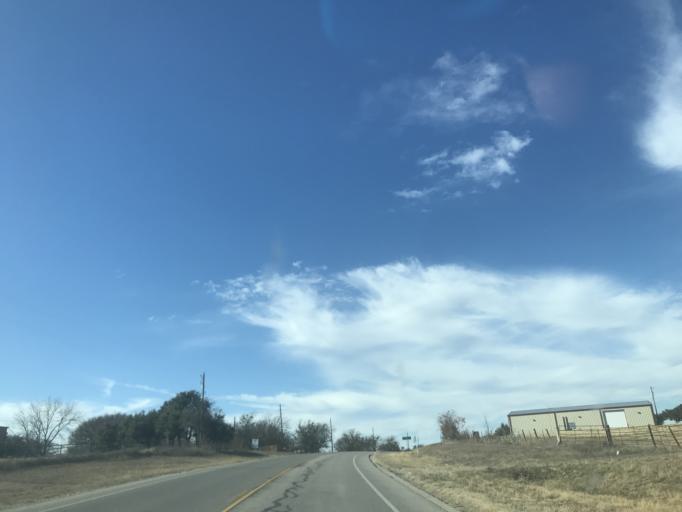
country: US
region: Texas
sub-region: Erath County
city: Stephenville
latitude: 32.2071
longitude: -98.1917
